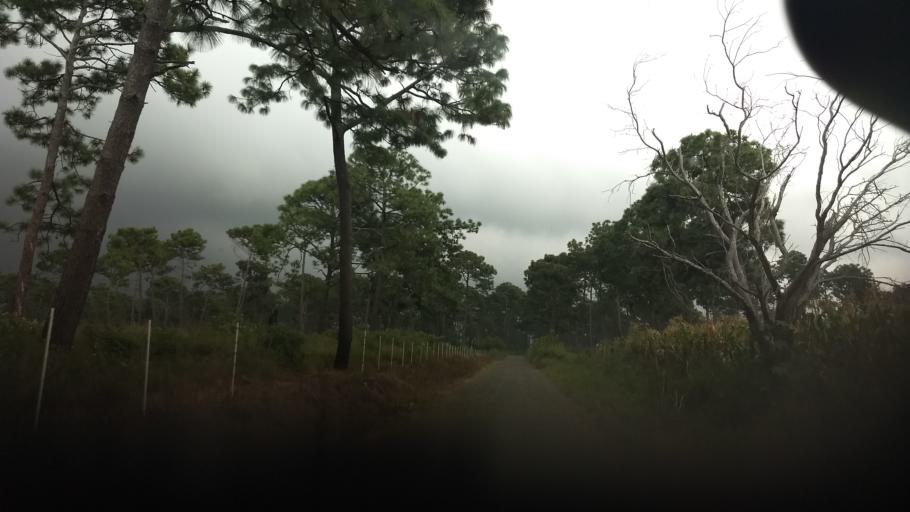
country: MX
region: Jalisco
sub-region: Tonila
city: San Marcos
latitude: 19.4650
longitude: -103.5295
